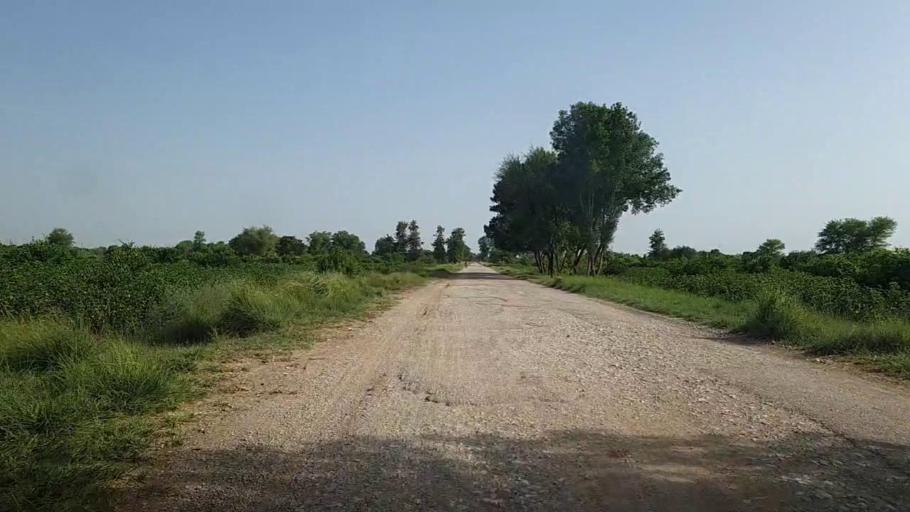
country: PK
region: Sindh
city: Karaundi
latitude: 26.8635
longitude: 68.3309
